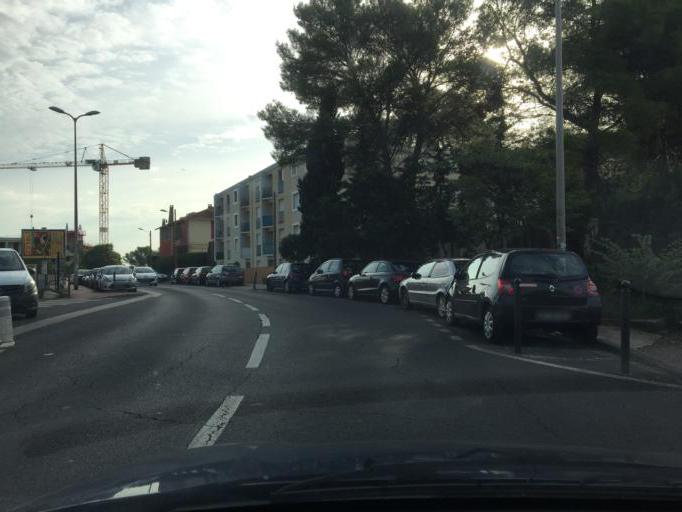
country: FR
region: Languedoc-Roussillon
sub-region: Departement de l'Herault
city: Montpellier
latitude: 43.6352
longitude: 3.8709
